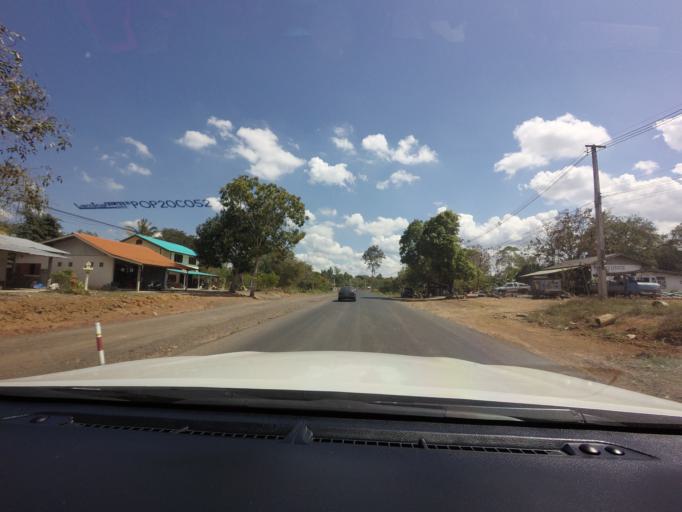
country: TH
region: Nakhon Ratchasima
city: Wang Nam Khiao
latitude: 14.3662
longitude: 101.8924
